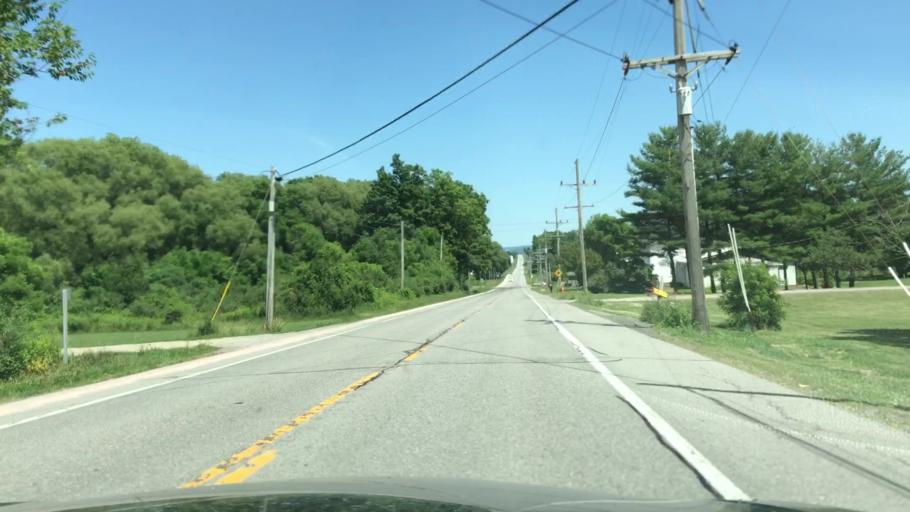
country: US
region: New York
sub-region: Wyoming County
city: Perry
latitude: 42.7495
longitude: -77.9940
